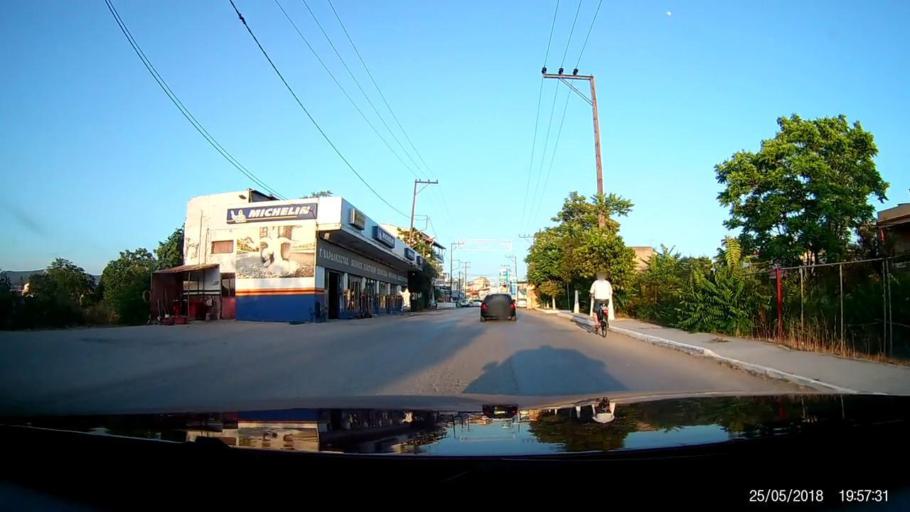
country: GR
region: Central Greece
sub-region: Nomos Evvoias
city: Vasilikon
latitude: 38.4263
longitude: 23.6674
